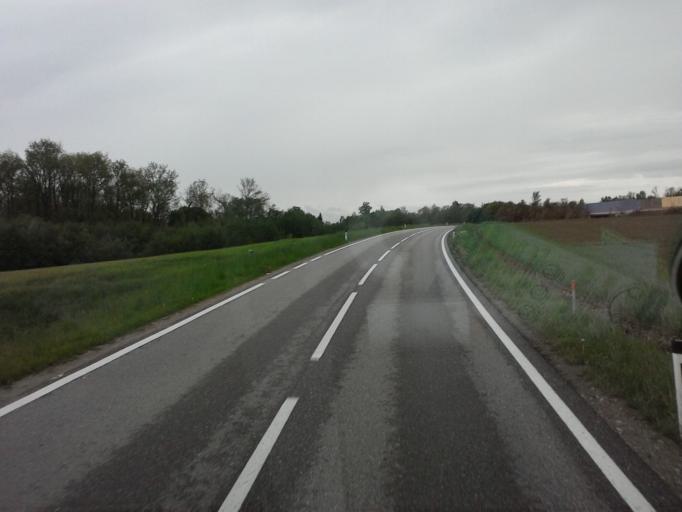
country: AT
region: Upper Austria
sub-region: Politischer Bezirk Scharding
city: Sankt Marienkirchen bei Schaerding
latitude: 48.3731
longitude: 13.4157
